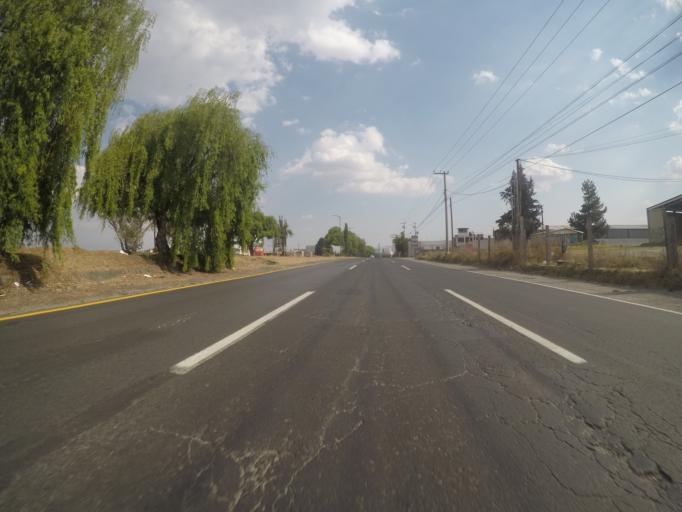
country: MX
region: Morelos
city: San Miguel Totocuitlapilco
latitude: 19.2223
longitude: -99.5931
